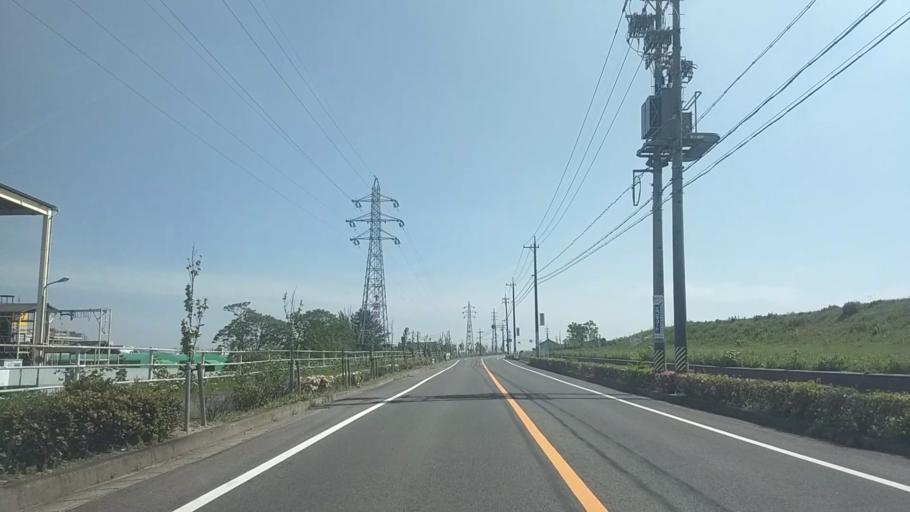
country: JP
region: Aichi
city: Okazaki
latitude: 34.9780
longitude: 137.1503
